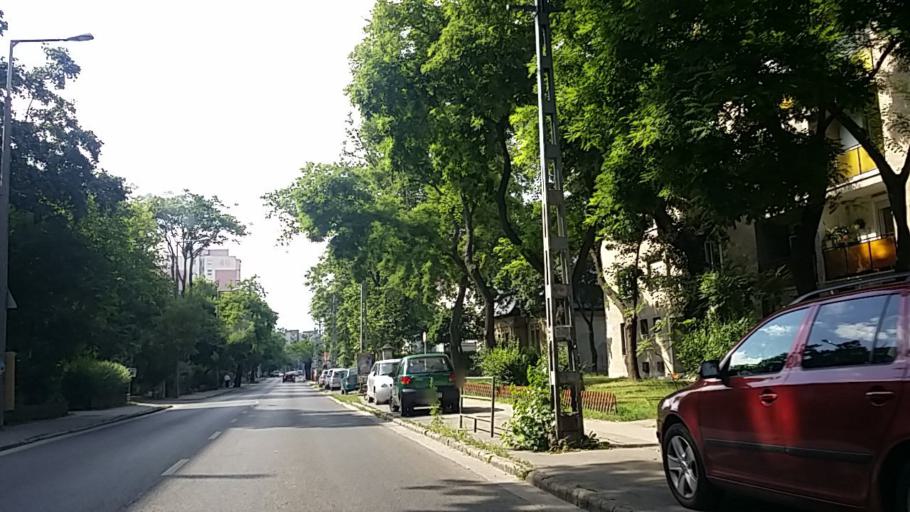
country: HU
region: Budapest
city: Budapest XX. keruelet
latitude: 47.4342
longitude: 19.1013
